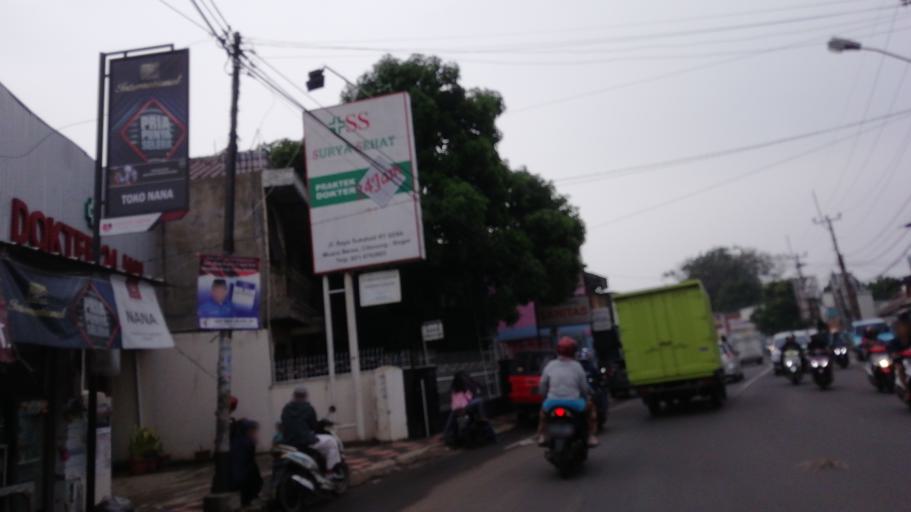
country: ID
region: West Java
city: Cibinong
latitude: -6.4935
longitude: 106.8124
